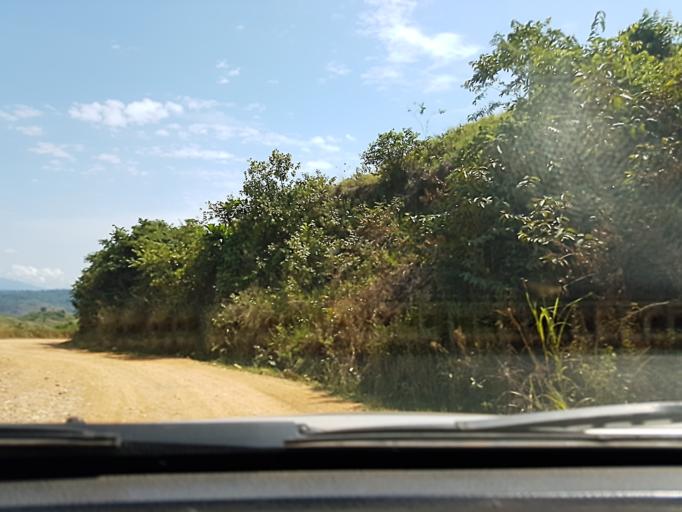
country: RW
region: Western Province
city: Cyangugu
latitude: -2.7030
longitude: 28.9139
